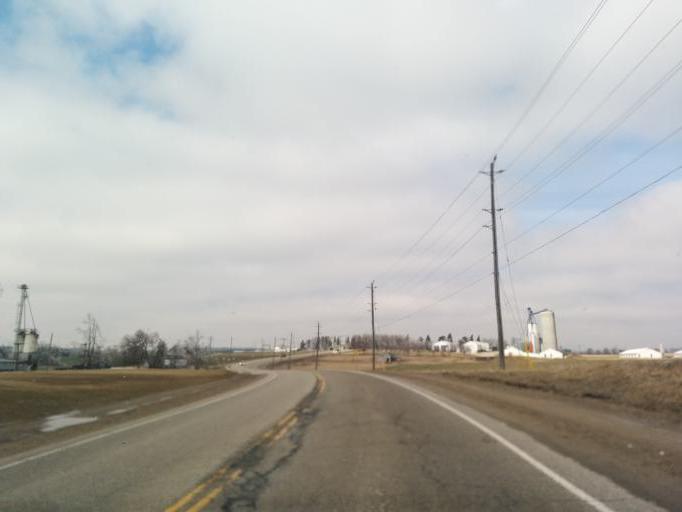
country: CA
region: Ontario
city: Waterloo
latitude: 43.6081
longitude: -80.5527
